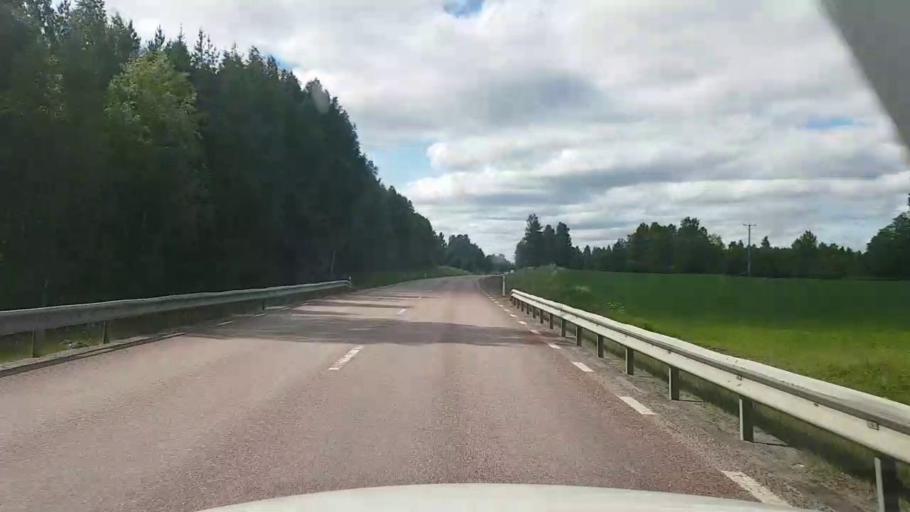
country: SE
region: Gaevleborg
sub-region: Ljusdals Kommun
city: Ljusdal
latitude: 61.8084
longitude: 16.0969
